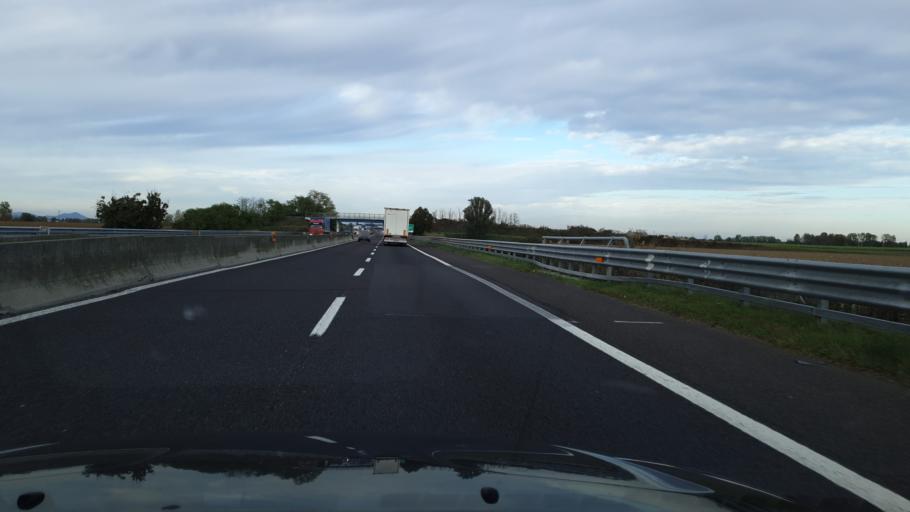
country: IT
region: Veneto
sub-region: Provincia di Rovigo
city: Costa di Rovigo
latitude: 45.0366
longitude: 11.7063
